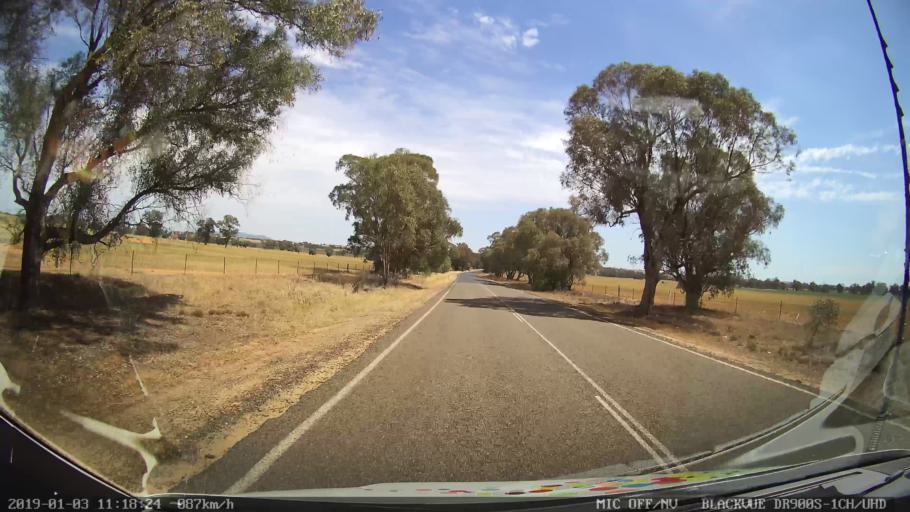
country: AU
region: New South Wales
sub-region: Young
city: Young
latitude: -34.1264
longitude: 148.2627
